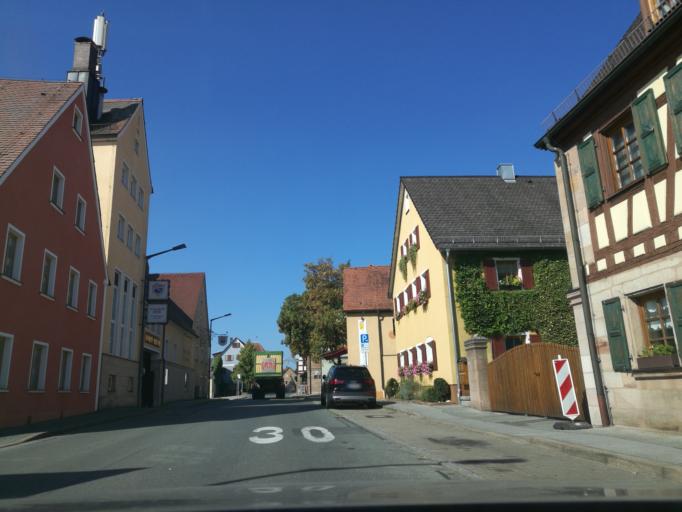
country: DE
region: Bavaria
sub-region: Regierungsbezirk Mittelfranken
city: Ammerndorf
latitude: 49.4211
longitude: 10.8525
